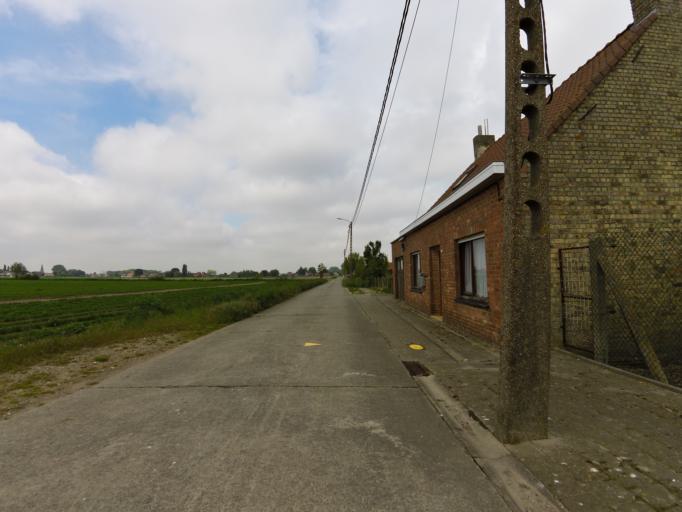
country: BE
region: Flanders
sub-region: Provincie West-Vlaanderen
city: Koekelare
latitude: 51.1176
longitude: 2.9737
